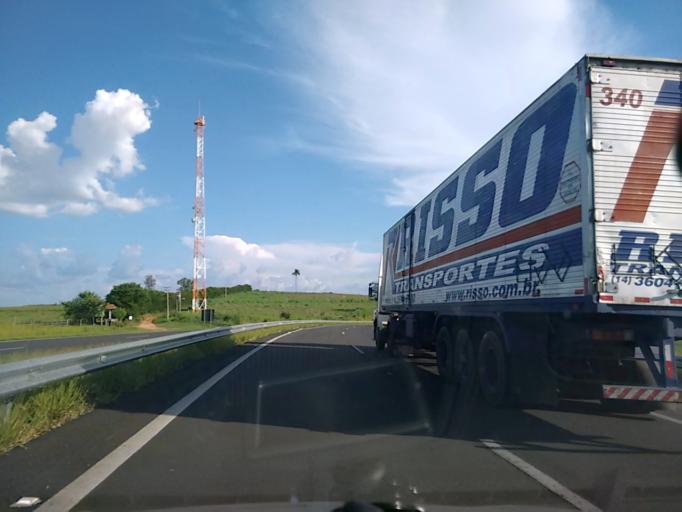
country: BR
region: Sao Paulo
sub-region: Duartina
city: Duartina
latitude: -22.2847
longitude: -49.4921
